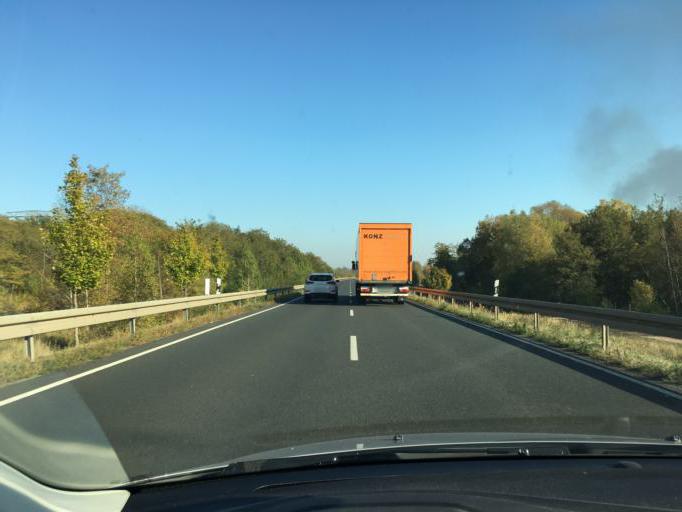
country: DE
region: Saxony-Anhalt
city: Sandersdorf
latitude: 51.6443
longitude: 12.2552
